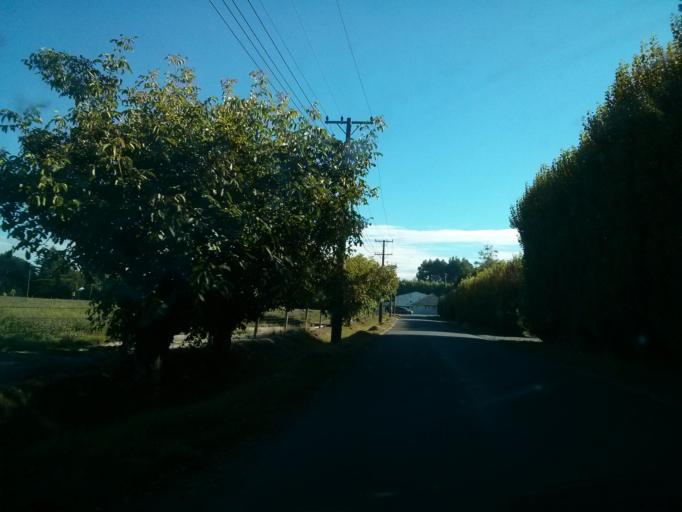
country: NZ
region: Canterbury
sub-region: Christchurch City
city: Christchurch
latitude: -43.4811
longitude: 172.5620
